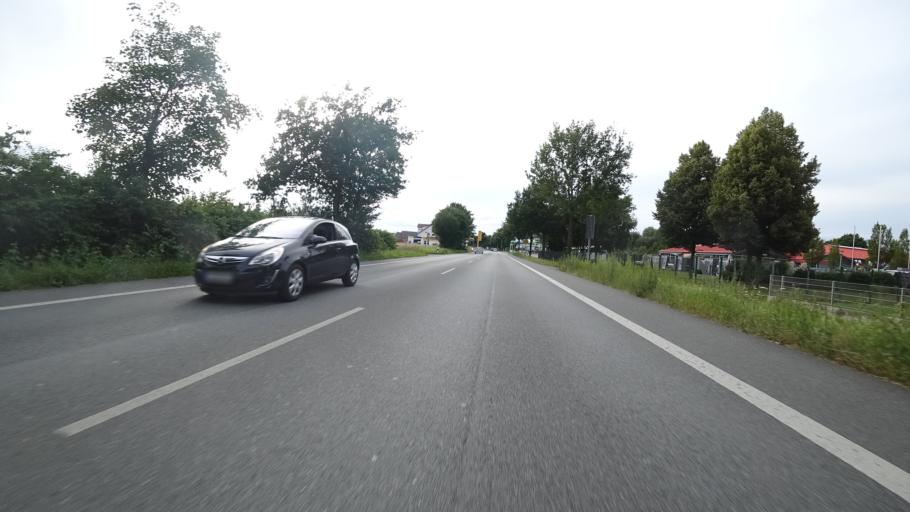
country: DE
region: North Rhine-Westphalia
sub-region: Regierungsbezirk Detmold
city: Harsewinkel
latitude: 51.9545
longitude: 8.2434
